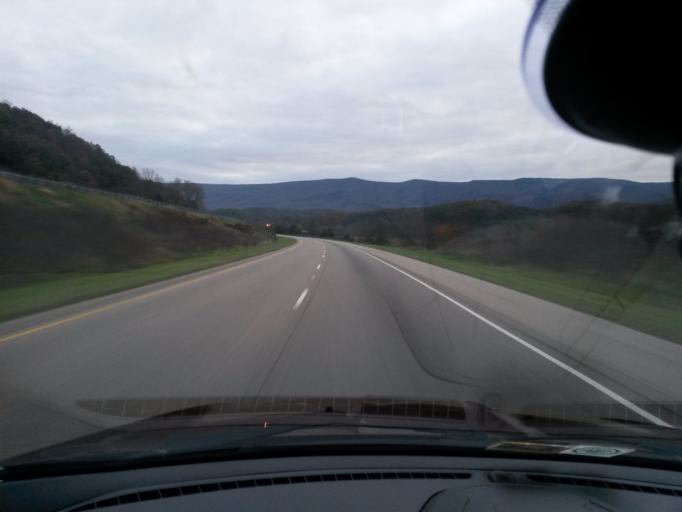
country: US
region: Virginia
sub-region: Alleghany County
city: Clifton Forge
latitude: 37.7954
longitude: -79.7216
